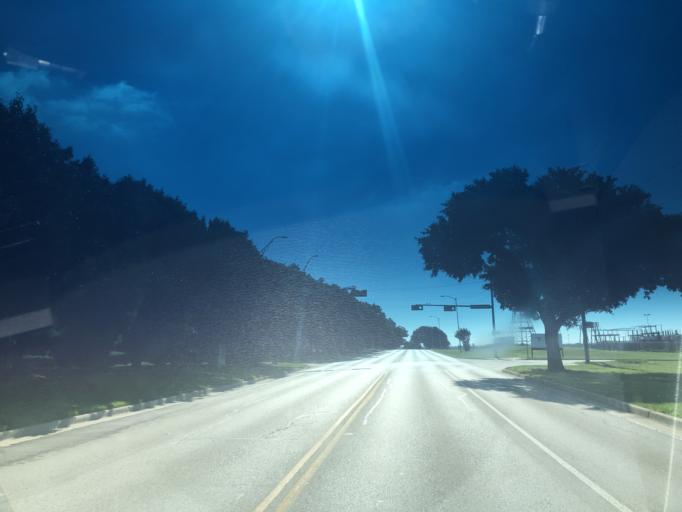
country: US
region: Texas
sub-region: Dallas County
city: Grand Prairie
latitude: 32.7205
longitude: -97.0335
